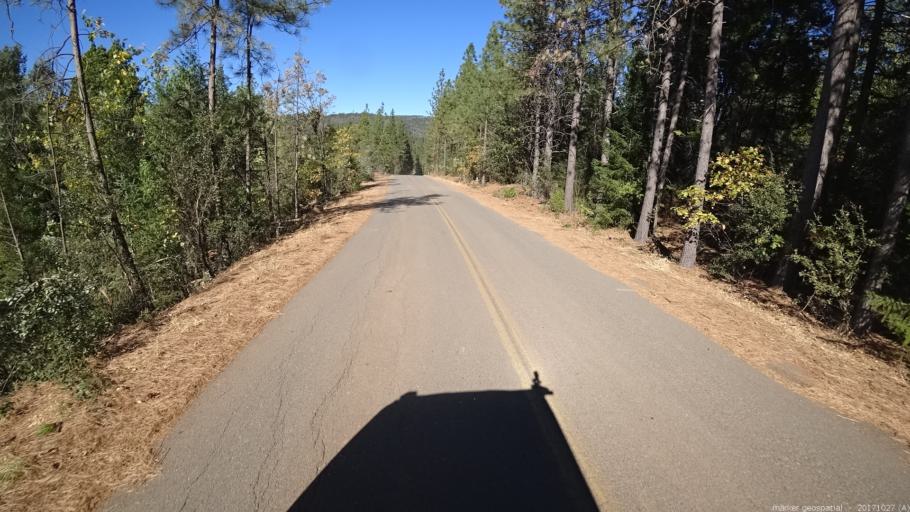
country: US
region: California
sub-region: Shasta County
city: Shingletown
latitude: 40.6664
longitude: -121.8834
